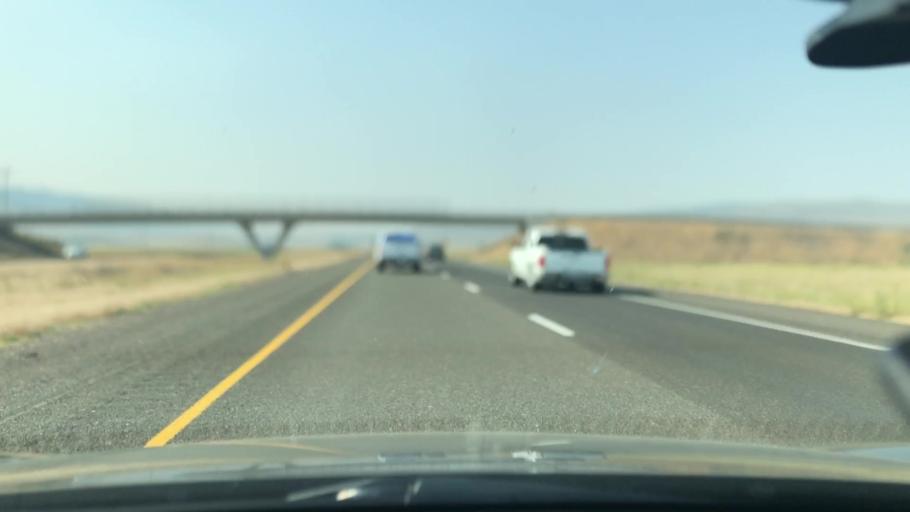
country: US
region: Oregon
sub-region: Union County
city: Union
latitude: 45.0971
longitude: -117.9527
